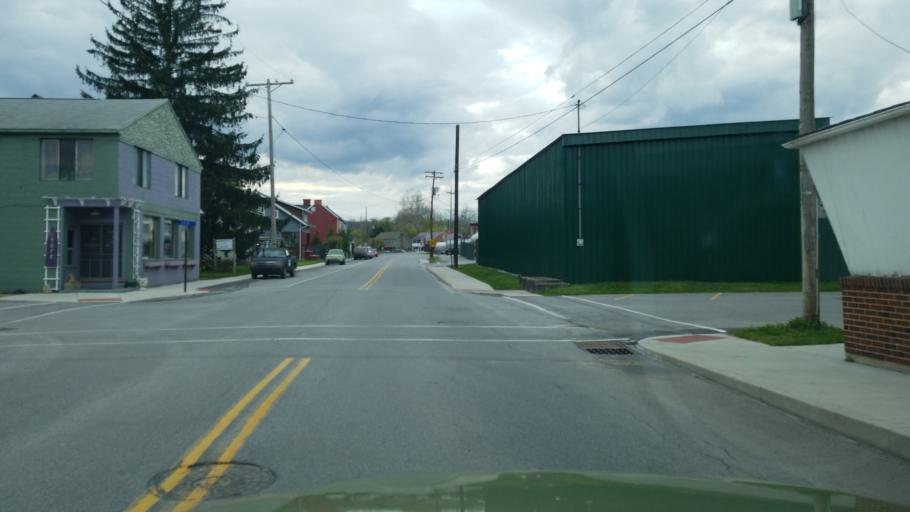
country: US
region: Pennsylvania
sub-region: Blair County
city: Hollidaysburg
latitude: 40.4262
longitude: -78.3963
